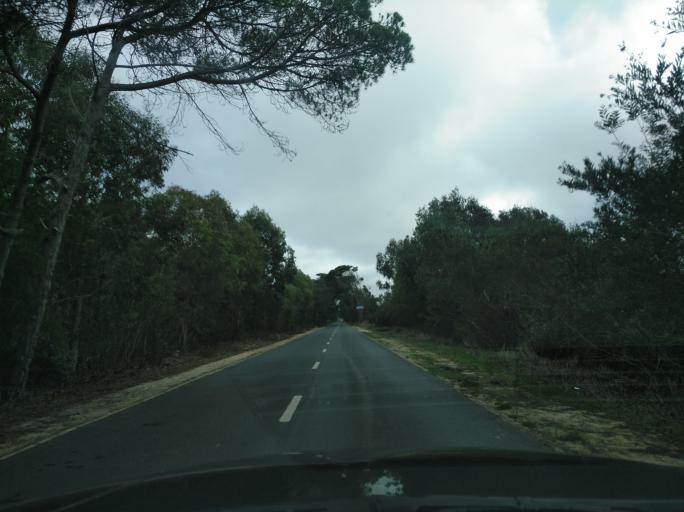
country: PT
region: Beja
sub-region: Odemira
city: Vila Nova de Milfontes
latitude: 37.7129
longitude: -8.7785
